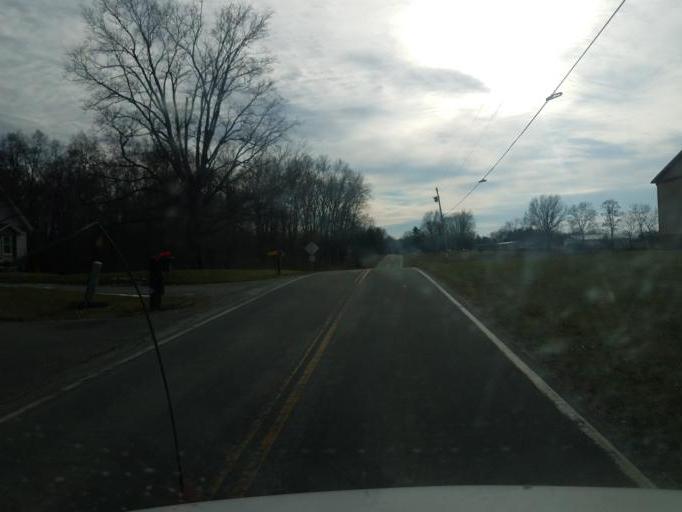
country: US
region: Ohio
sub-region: Delaware County
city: Delaware
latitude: 40.2956
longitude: -82.9650
